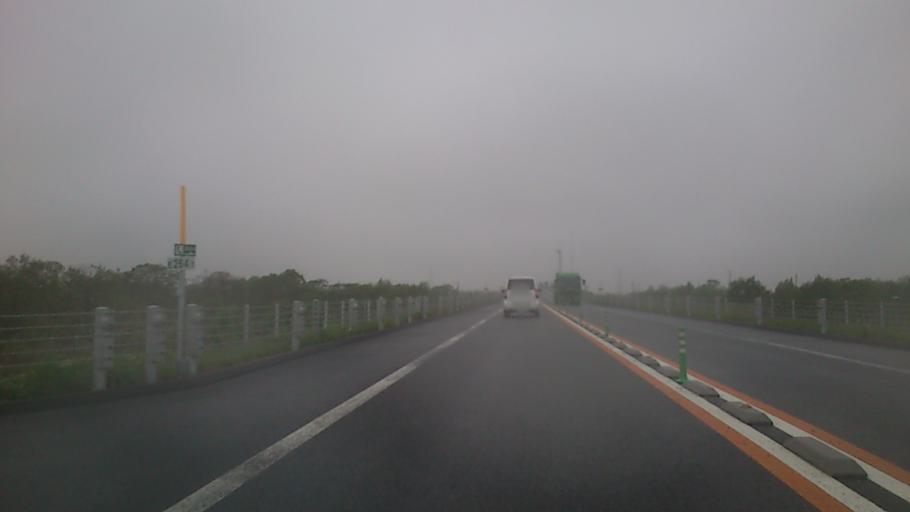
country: JP
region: Hokkaido
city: Kushiro
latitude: 43.0326
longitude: 144.3925
